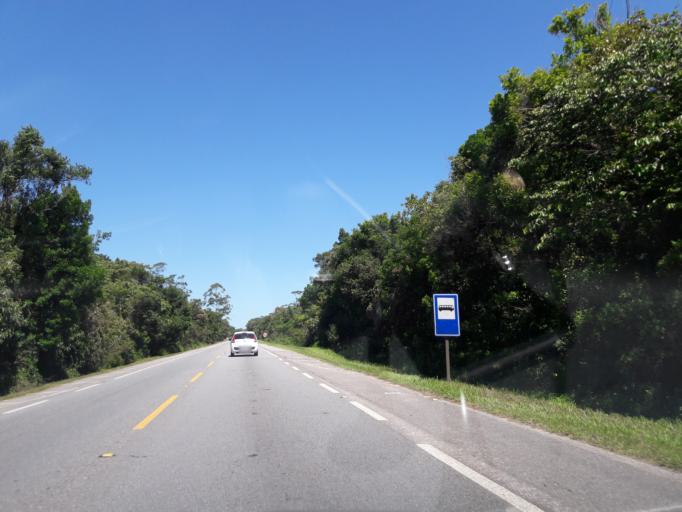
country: BR
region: Parana
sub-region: Pontal Do Parana
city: Pontal do Parana
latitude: -25.6618
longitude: -48.5204
